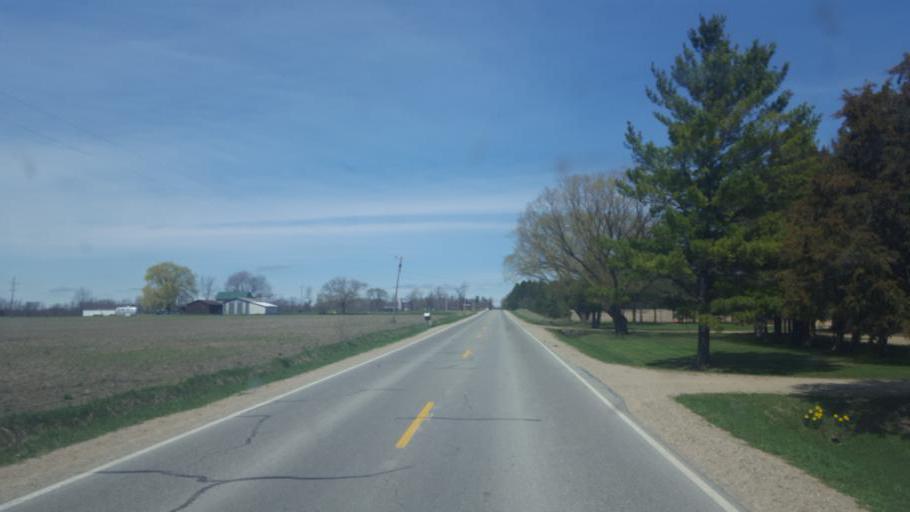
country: US
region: Michigan
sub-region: Gladwin County
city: Gladwin
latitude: 43.9342
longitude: -84.5852
